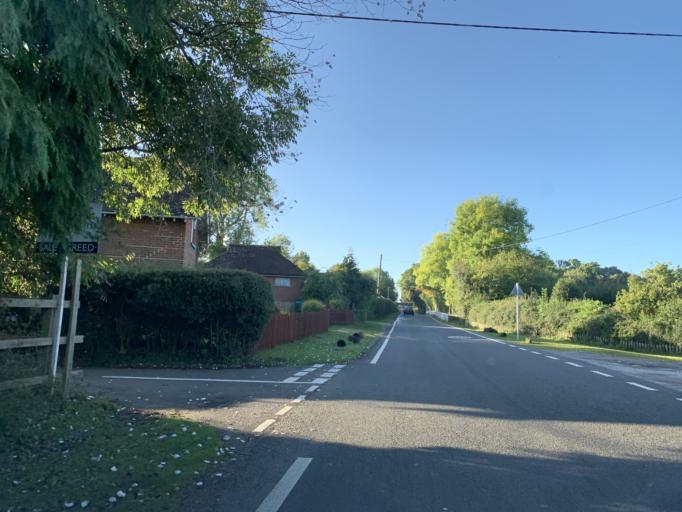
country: GB
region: England
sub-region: Hampshire
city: Cadnam
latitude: 50.9430
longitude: -1.6178
